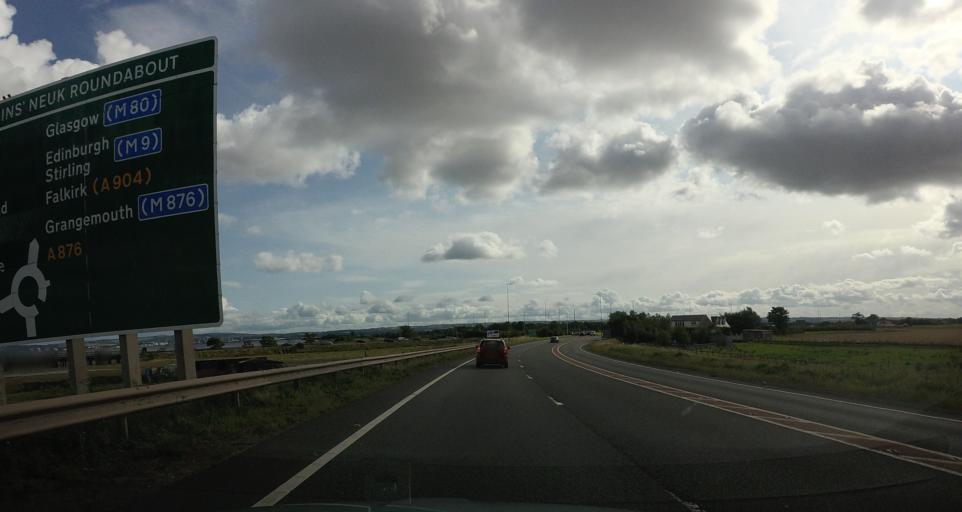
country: GB
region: Scotland
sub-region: Fife
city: Kincardine
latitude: 56.0646
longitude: -3.7359
